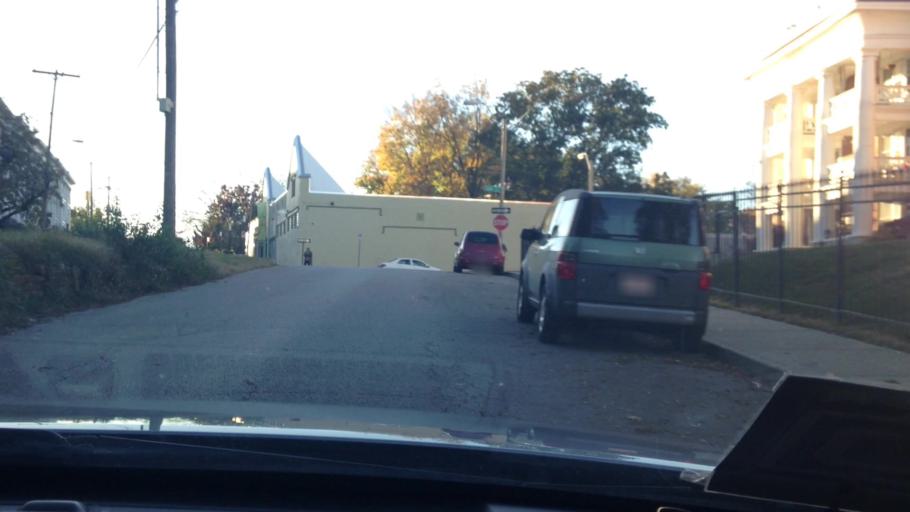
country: US
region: Kansas
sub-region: Johnson County
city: Westwood
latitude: 39.0492
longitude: -94.5812
